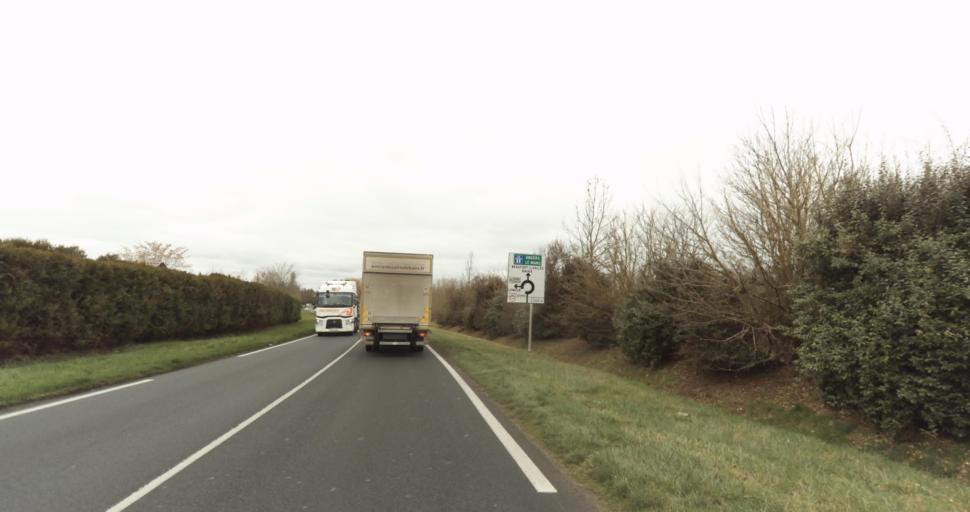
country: FR
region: Pays de la Loire
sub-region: Departement de Maine-et-Loire
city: Jumelles
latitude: 47.3808
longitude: -0.1038
